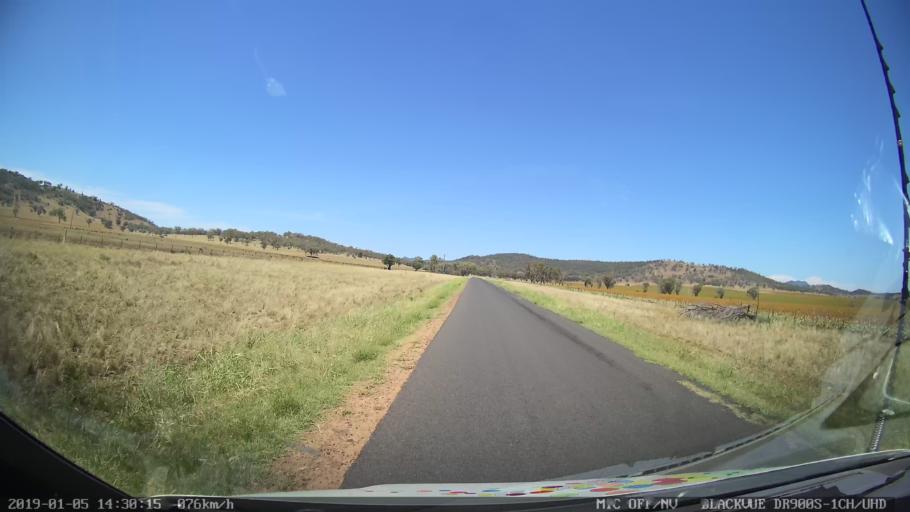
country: AU
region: New South Wales
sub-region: Tamworth Municipality
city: Phillip
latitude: -31.2280
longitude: 150.5902
